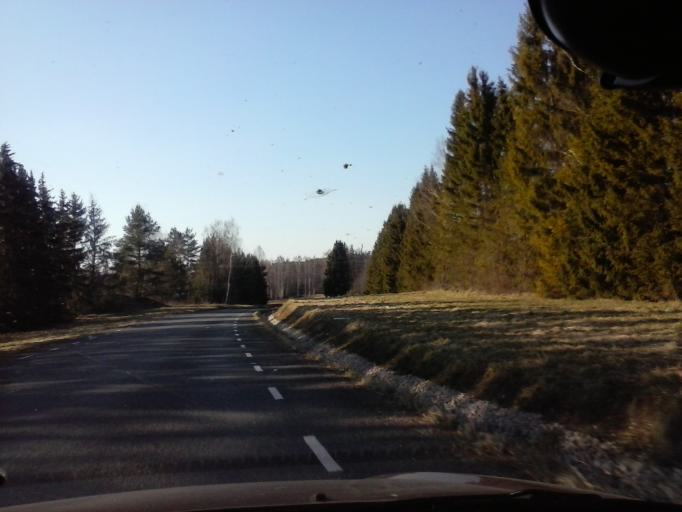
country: EE
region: Tartu
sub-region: UElenurme vald
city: Ulenurme
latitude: 58.1708
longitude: 26.8355
